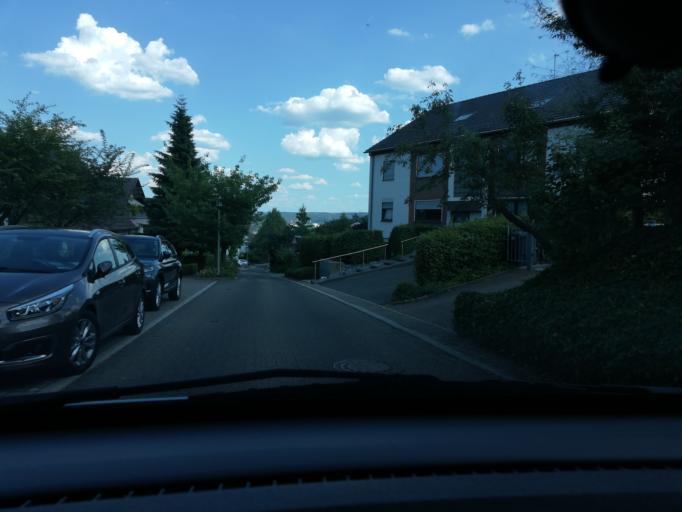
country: DE
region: North Rhine-Westphalia
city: Witten
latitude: 51.4025
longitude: 7.3296
